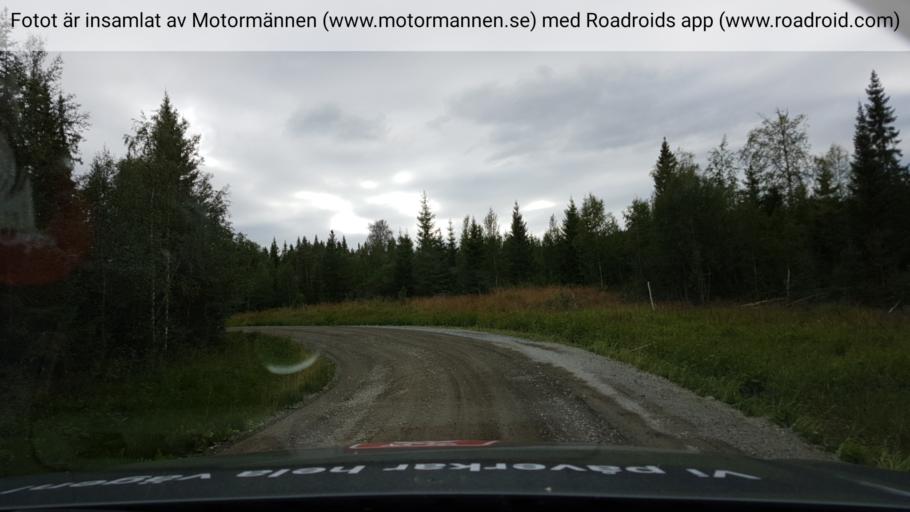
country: SE
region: Jaemtland
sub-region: Krokoms Kommun
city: Valla
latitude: 63.4015
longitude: 14.0761
